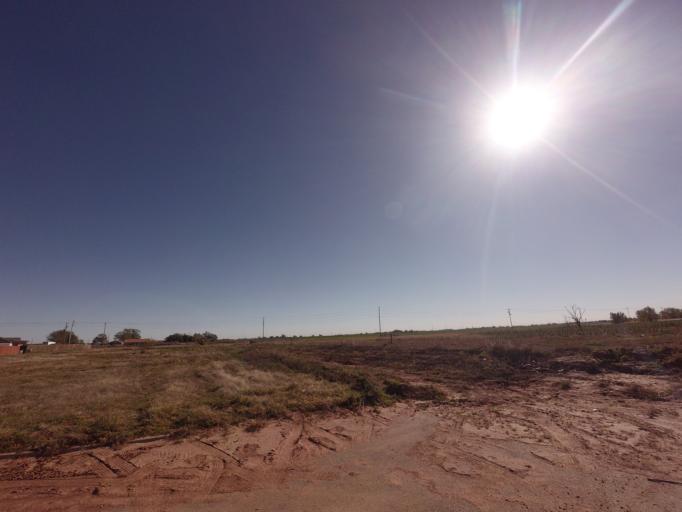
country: US
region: New Mexico
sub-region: Curry County
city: Clovis
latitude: 34.4123
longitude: -103.1624
